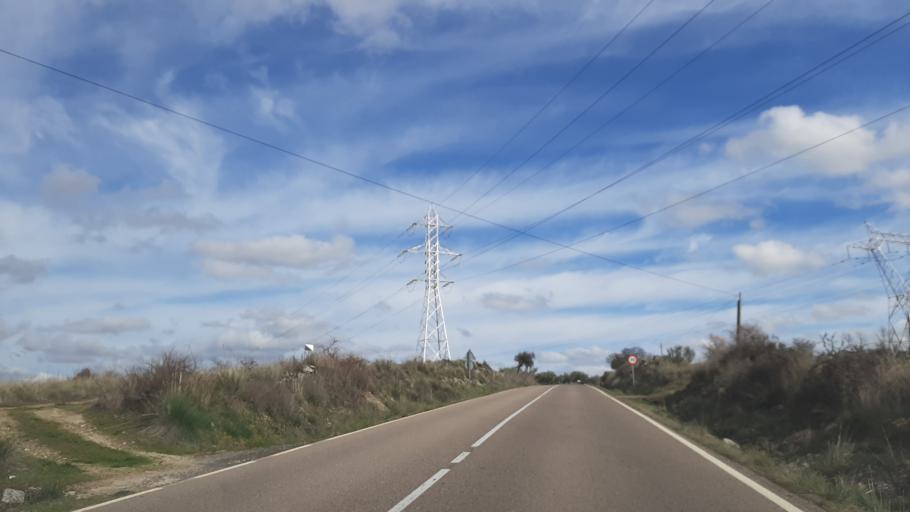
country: ES
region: Castille and Leon
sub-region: Provincia de Salamanca
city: Villarino de los Aires
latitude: 41.2640
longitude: -6.4496
